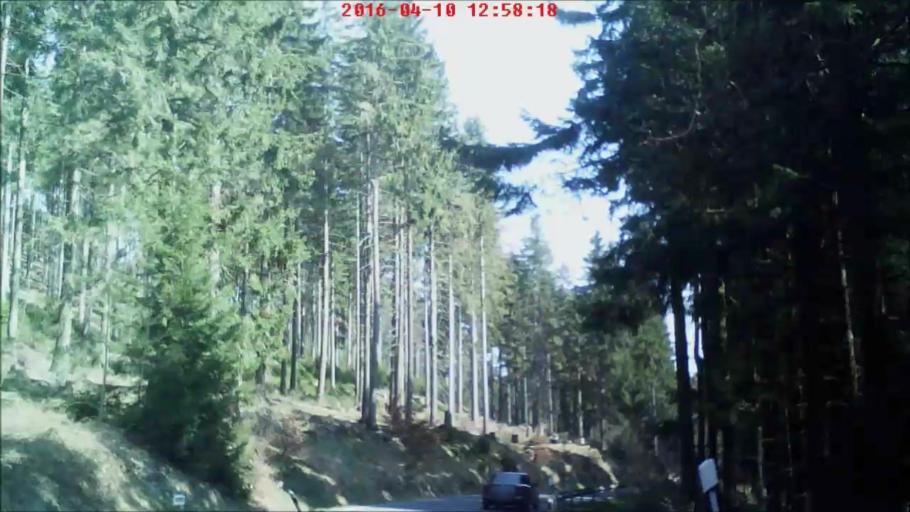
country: DE
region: Thuringia
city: Friedrichroda
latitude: 50.8359
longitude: 10.5340
